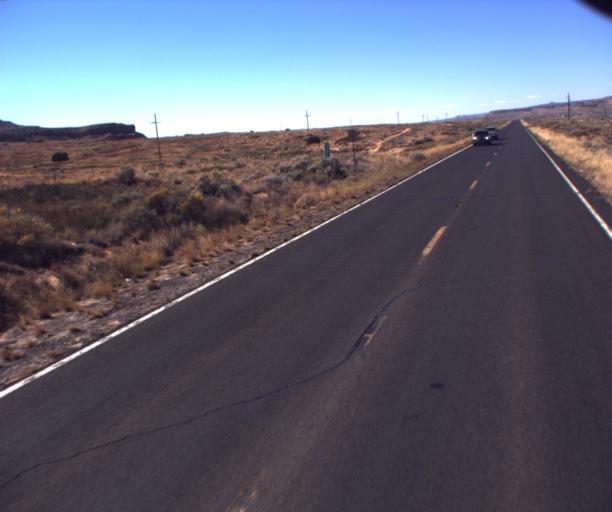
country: US
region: Arizona
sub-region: Navajo County
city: First Mesa
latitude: 35.8729
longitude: -110.5612
